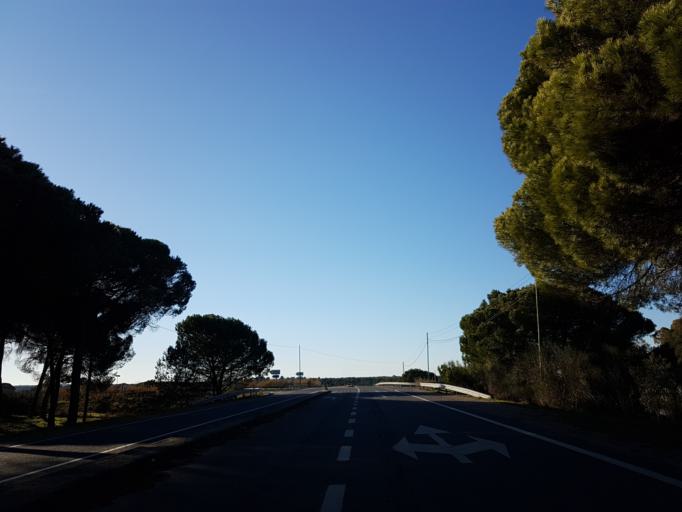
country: PT
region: Setubal
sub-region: Alcacer do Sal
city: Alcacer do Sal
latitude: 38.3611
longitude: -8.5195
